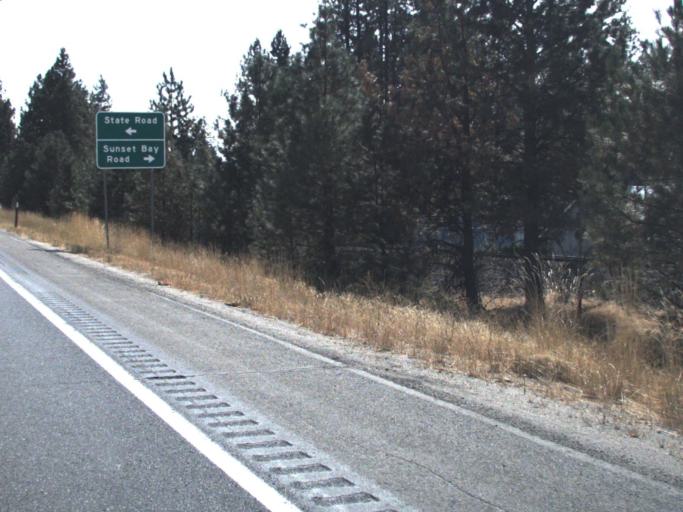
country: US
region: Washington
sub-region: Spokane County
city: Deer Park
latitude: 48.0559
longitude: -117.6174
